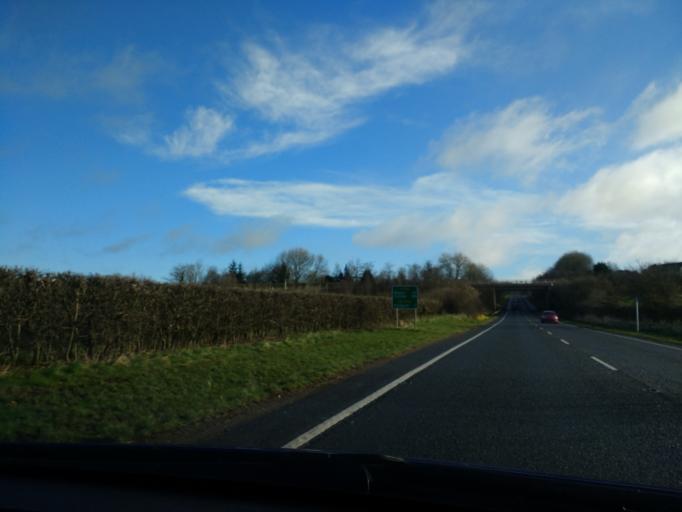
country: GB
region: England
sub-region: Cumbria
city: Cockermouth
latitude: 54.6700
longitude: -3.3896
